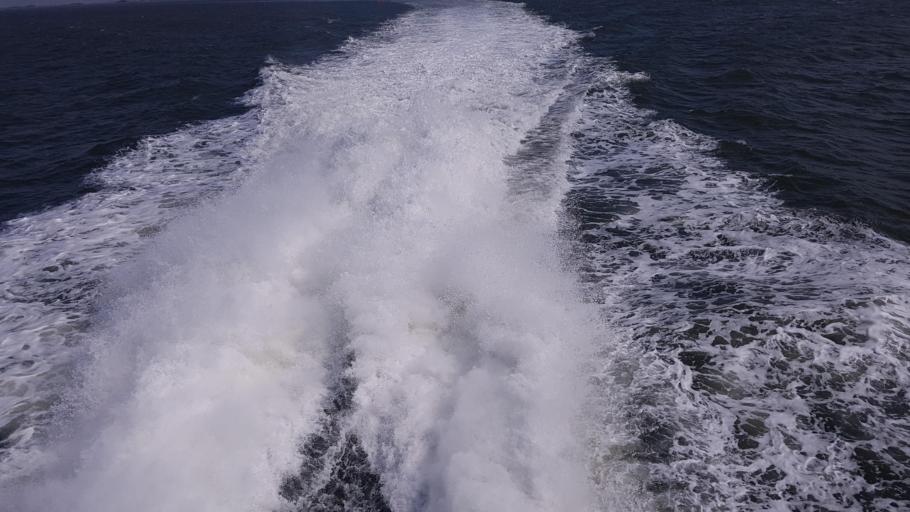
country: DE
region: Schleswig-Holstein
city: Osterhever
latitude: 54.4854
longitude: 8.7430
